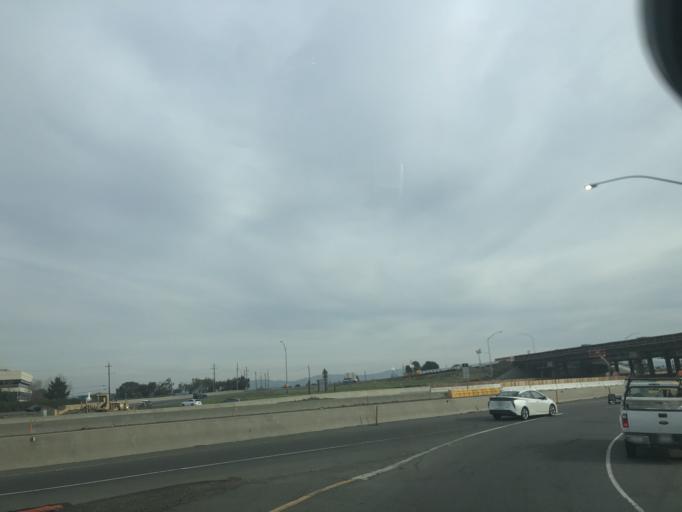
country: US
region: California
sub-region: Contra Costa County
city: Pacheco
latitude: 37.9952
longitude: -122.0714
